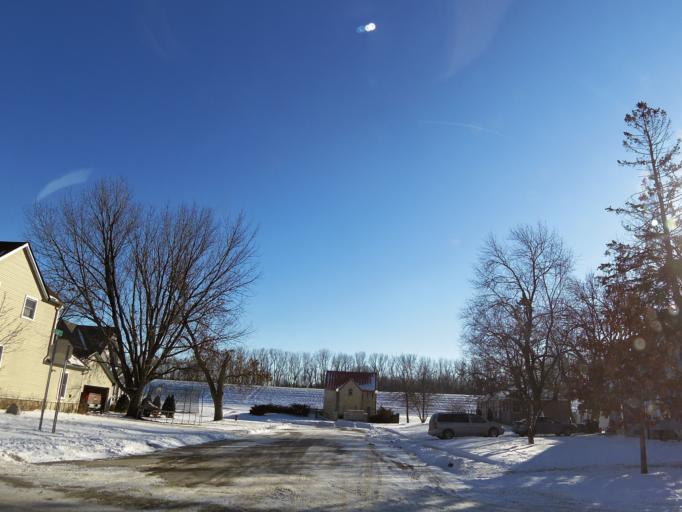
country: US
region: Minnesota
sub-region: Carver County
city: Chaska
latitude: 44.7849
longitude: -93.5972
